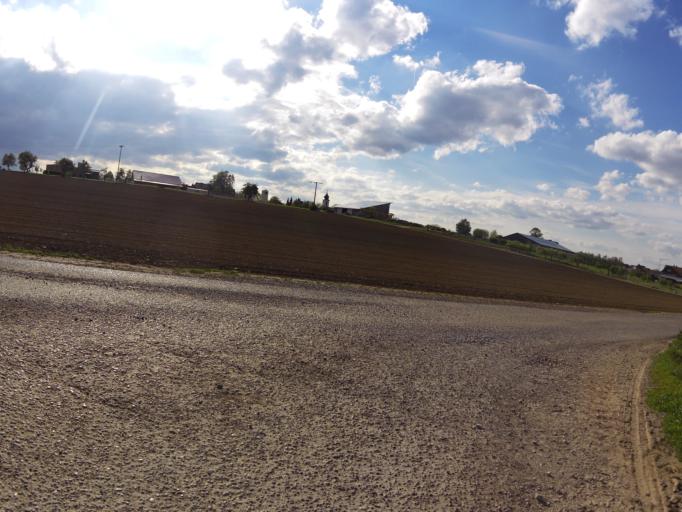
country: DE
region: Bavaria
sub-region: Regierungsbezirk Unterfranken
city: Unterpleichfeld
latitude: 49.8650
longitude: 10.0534
